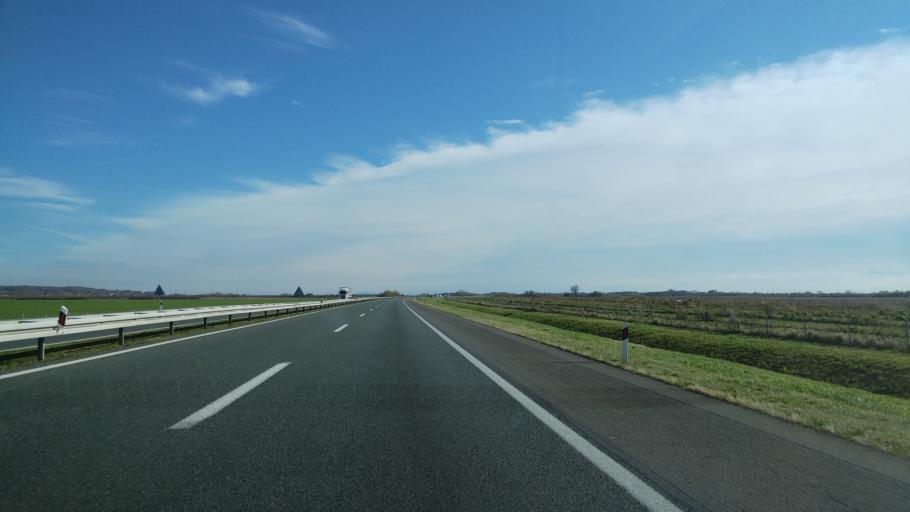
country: HR
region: Brodsko-Posavska
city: Okucani
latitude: 45.2643
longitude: 17.1551
